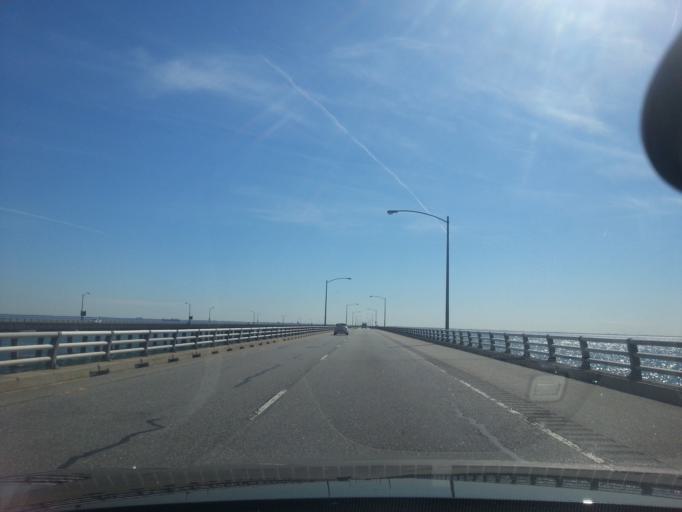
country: US
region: Virginia
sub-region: City of Virginia Beach
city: Virginia Beach
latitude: 37.0268
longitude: -76.0886
